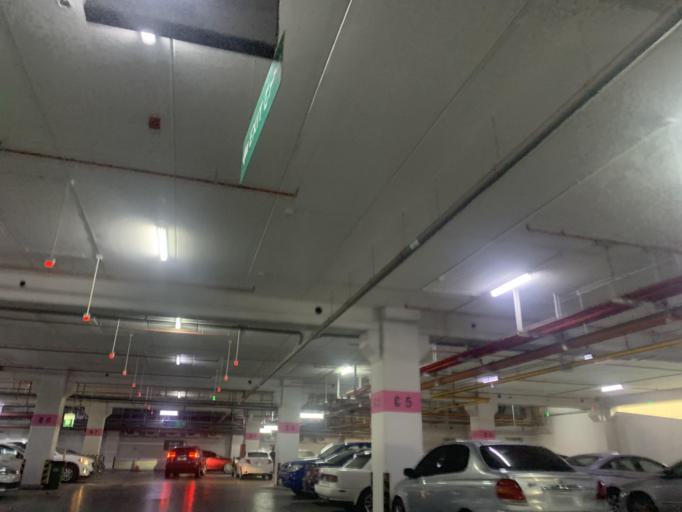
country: BH
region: Northern
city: Madinat `Isa
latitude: 26.1768
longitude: 50.4837
